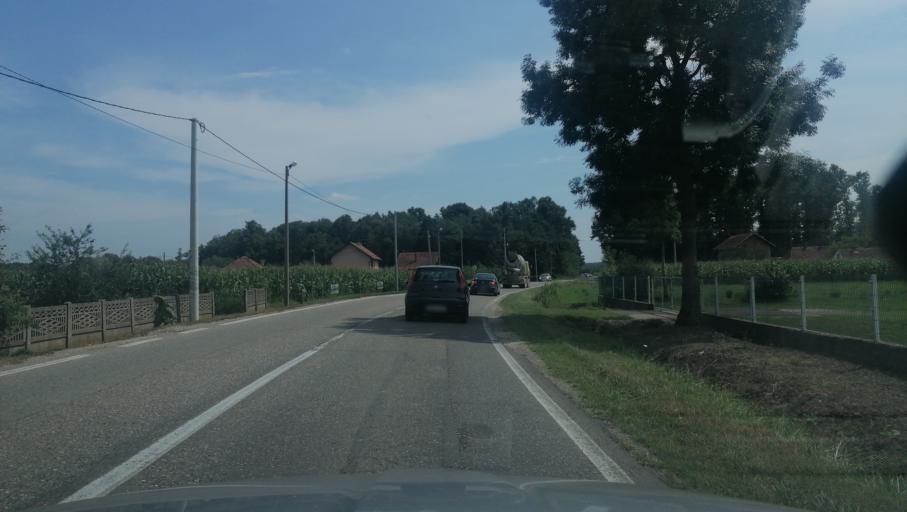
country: BA
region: Republika Srpska
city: Velika Obarska
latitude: 44.8216
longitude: 19.0494
